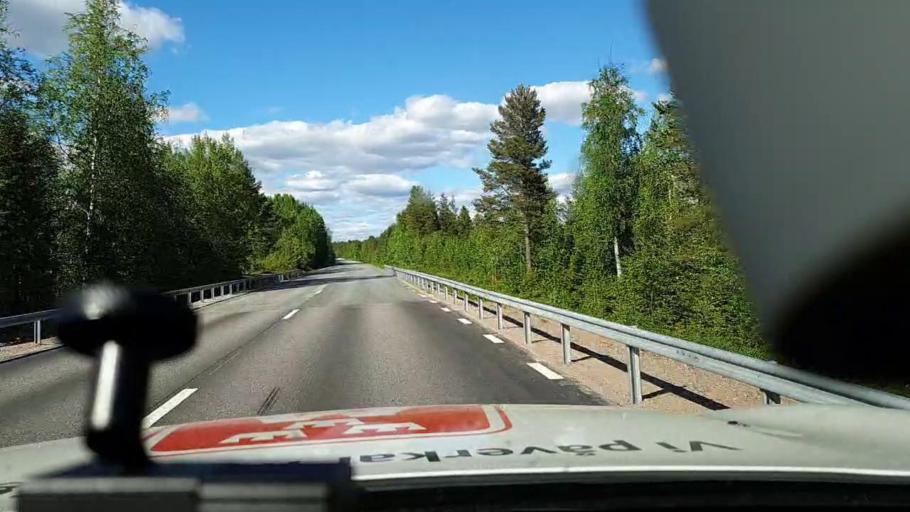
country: FI
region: Lapland
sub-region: Torniolaakso
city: Ylitornio
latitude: 66.3378
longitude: 23.6443
